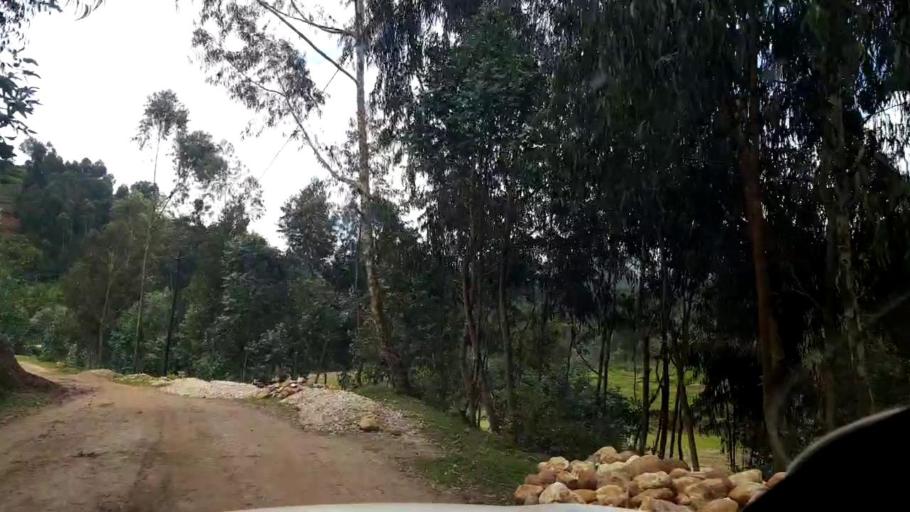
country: RW
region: Western Province
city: Kibuye
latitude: -1.9094
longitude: 29.4573
